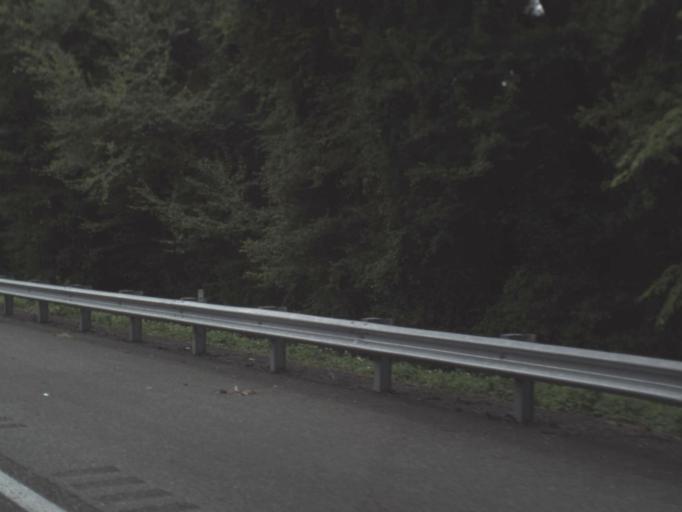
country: US
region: Florida
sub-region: Columbia County
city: Lake City
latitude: 30.0878
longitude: -82.6388
